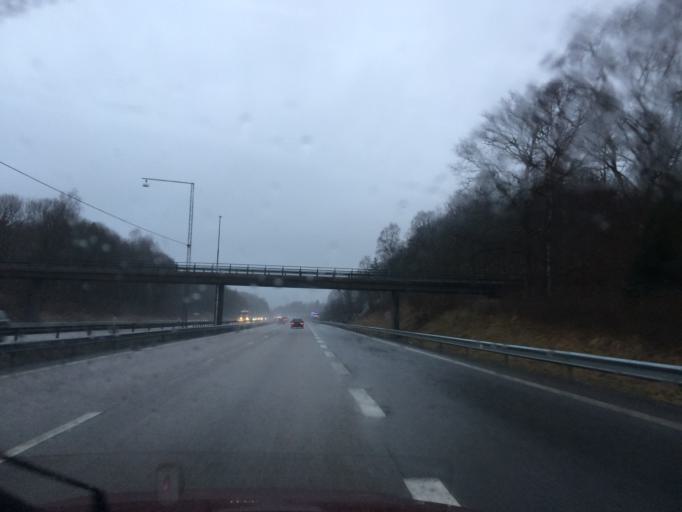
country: SE
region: Vaestra Goetaland
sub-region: Molndal
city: Lindome
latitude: 57.5782
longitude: 12.0613
